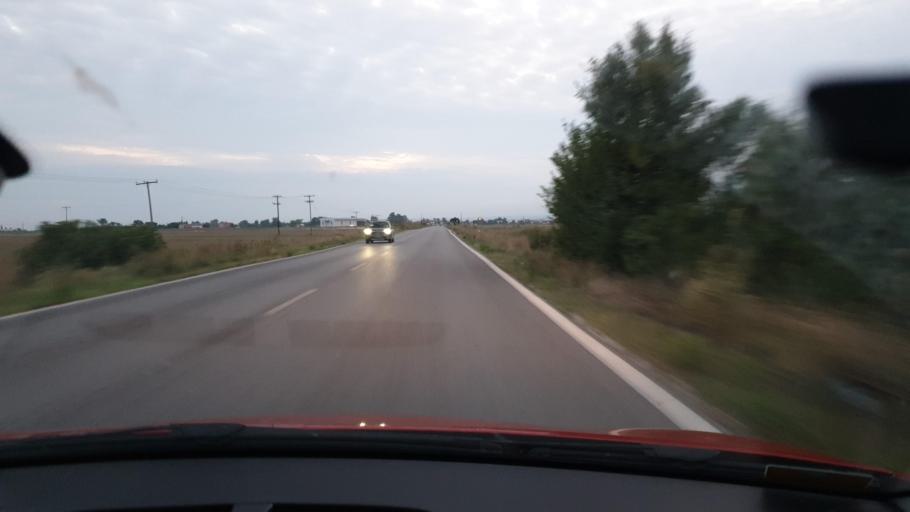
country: GR
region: Central Macedonia
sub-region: Nomos Kilkis
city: Polykastro
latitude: 40.9961
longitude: 22.6273
